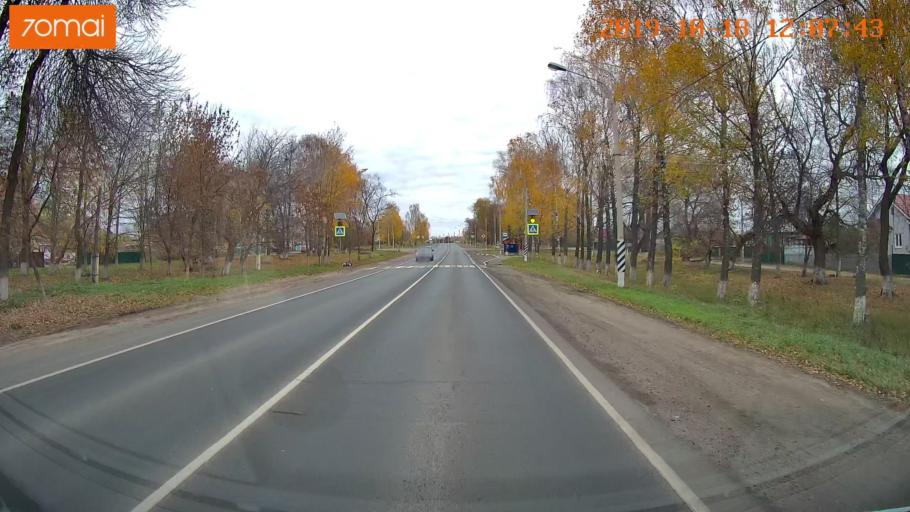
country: RU
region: Rjazan
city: Zakharovo
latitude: 54.3709
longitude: 39.2839
